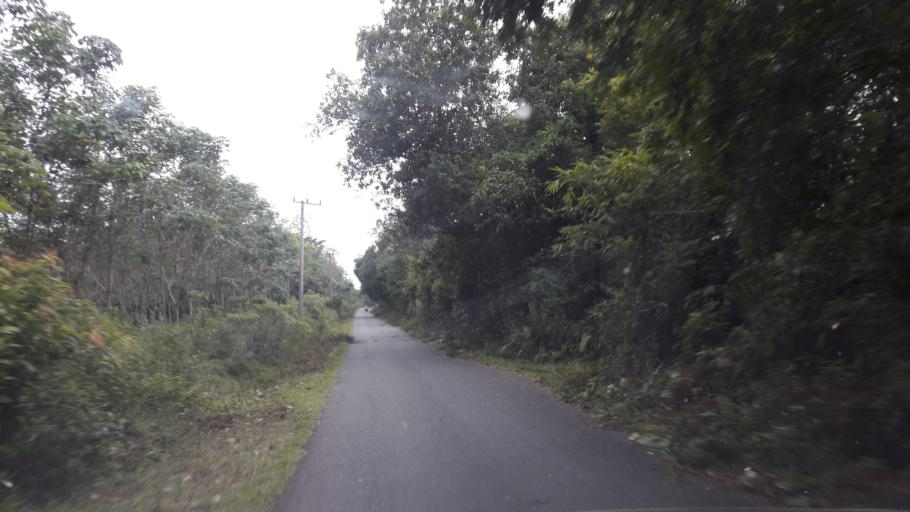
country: ID
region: South Sumatra
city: Gunungmenang
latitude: -3.1038
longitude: 104.0615
